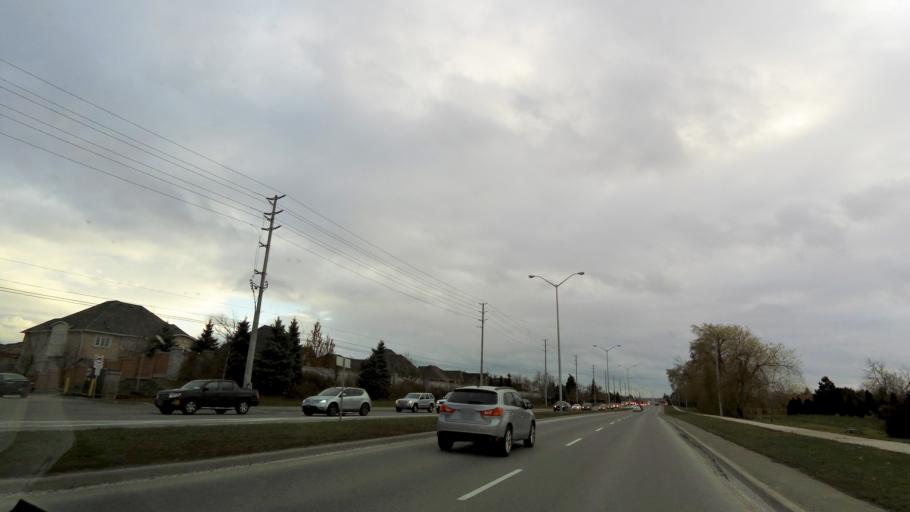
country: CA
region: Ontario
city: Brampton
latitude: 43.7818
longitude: -79.7013
